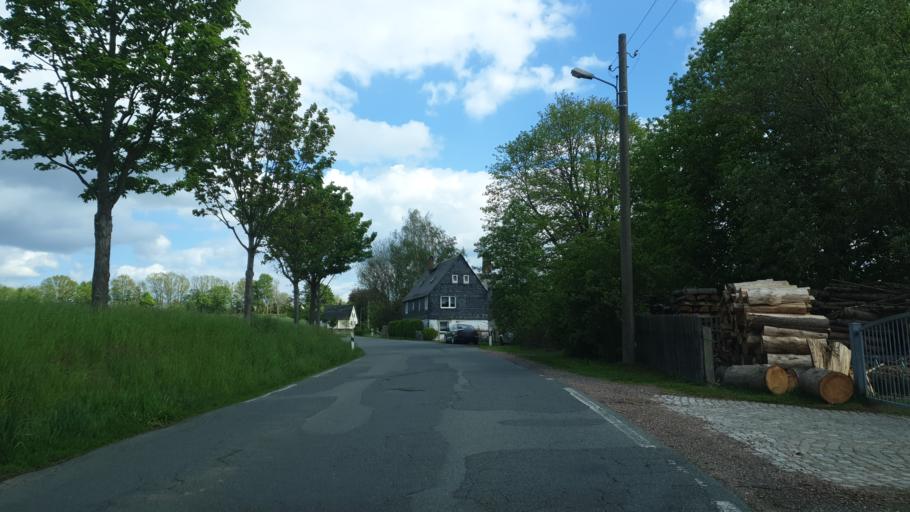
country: DE
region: Saxony
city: Niederdorf
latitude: 50.7764
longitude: 12.7841
